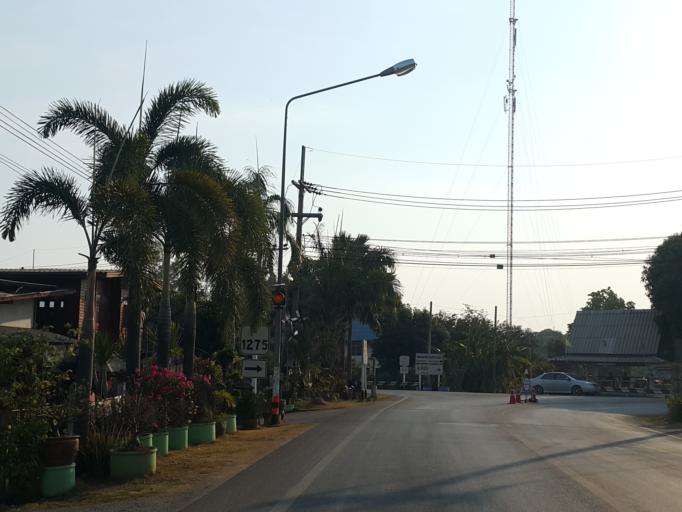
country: TH
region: Uttaradit
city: Phichai
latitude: 17.1638
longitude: 100.0987
